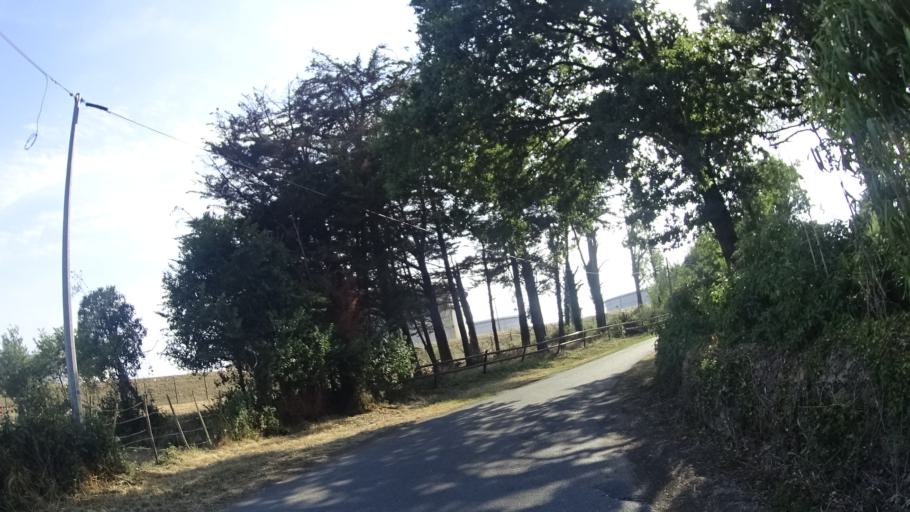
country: FR
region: Pays de la Loire
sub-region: Departement de la Loire-Atlantique
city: Donges
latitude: 47.3200
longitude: -2.0887
